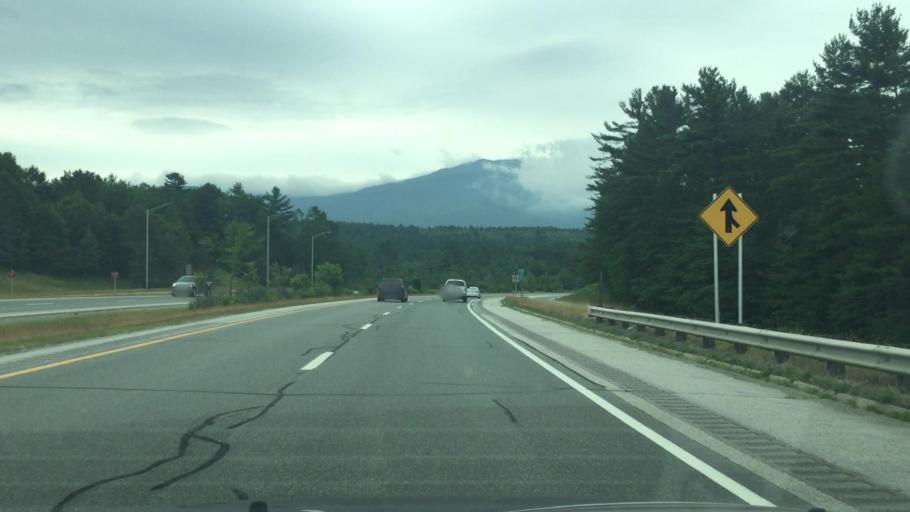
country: US
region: New Hampshire
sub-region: Grafton County
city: Littleton
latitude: 44.2219
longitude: -71.7329
